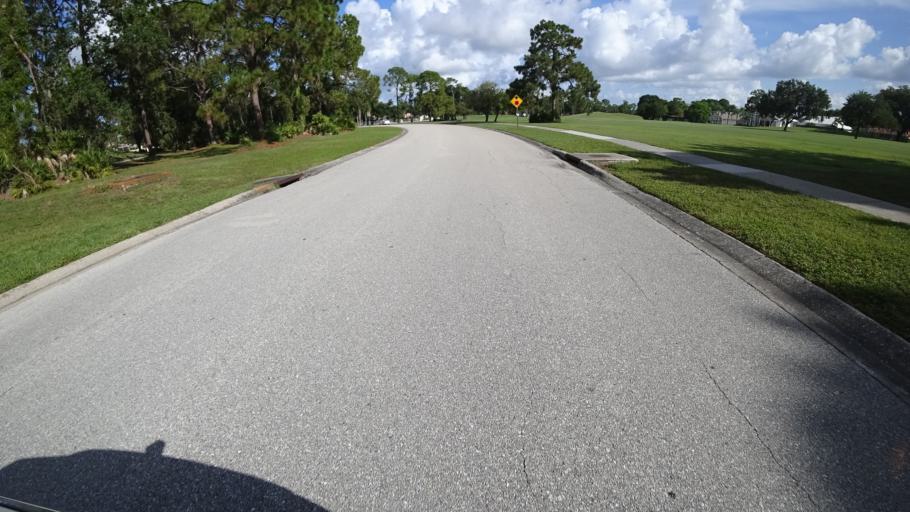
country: US
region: Florida
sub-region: Sarasota County
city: Desoto Lakes
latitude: 27.4038
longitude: -82.4857
